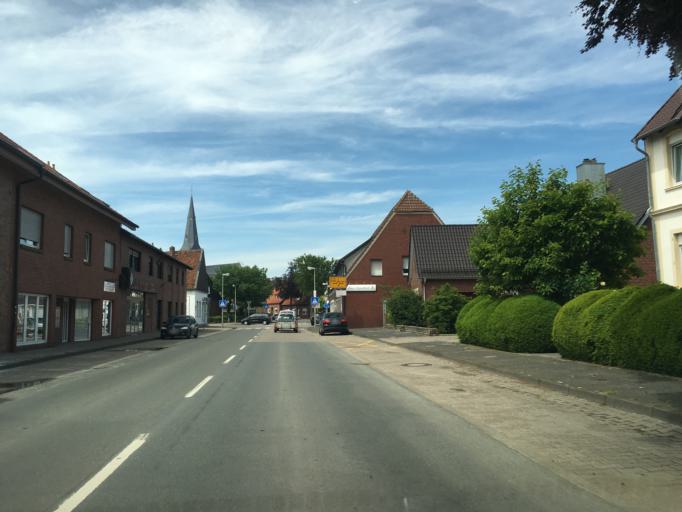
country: DE
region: North Rhine-Westphalia
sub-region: Regierungsbezirk Munster
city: Nordwalde
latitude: 52.0841
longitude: 7.4839
